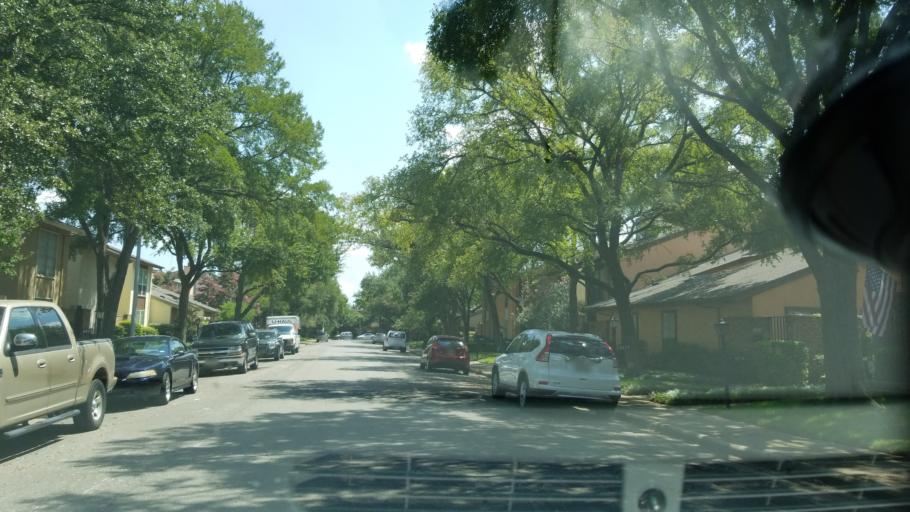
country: US
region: Texas
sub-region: Dallas County
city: Richardson
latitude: 32.9201
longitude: -96.7378
